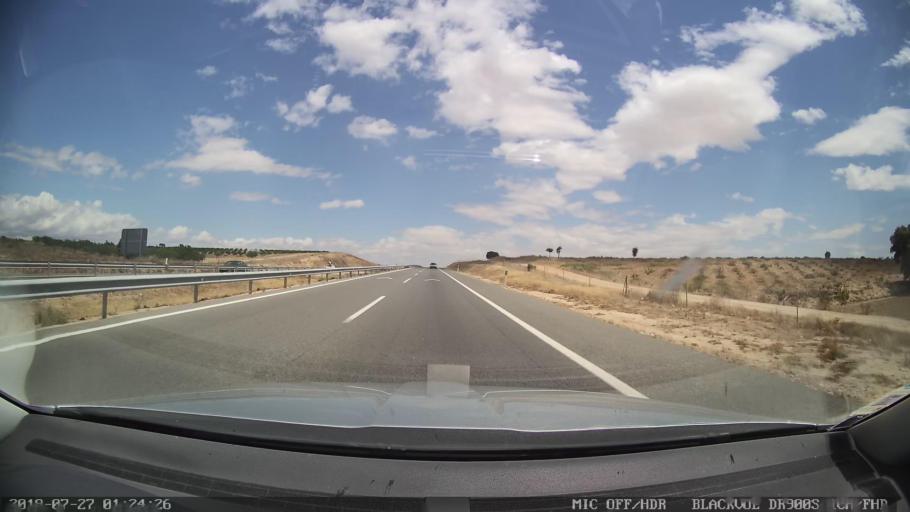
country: ES
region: Castille-La Mancha
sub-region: Province of Toledo
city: Santa Cruz del Retamar
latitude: 40.1313
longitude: -4.2091
